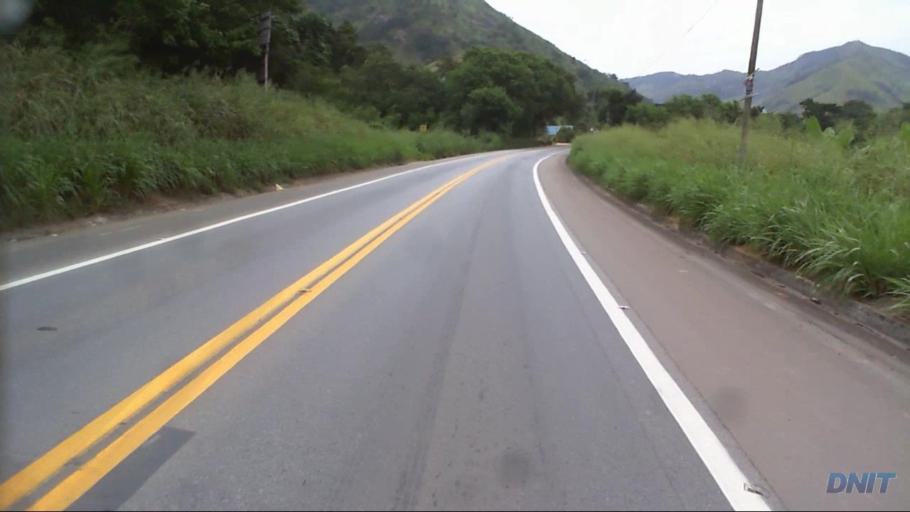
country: BR
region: Minas Gerais
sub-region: Timoteo
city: Timoteo
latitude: -19.5583
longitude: -42.7102
